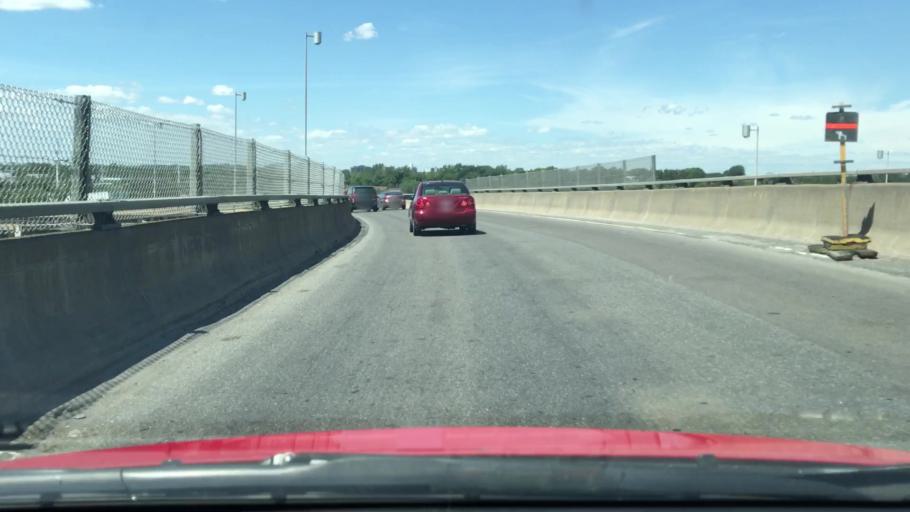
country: CA
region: Quebec
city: Montreal-Ouest
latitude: 45.4408
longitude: -73.6504
